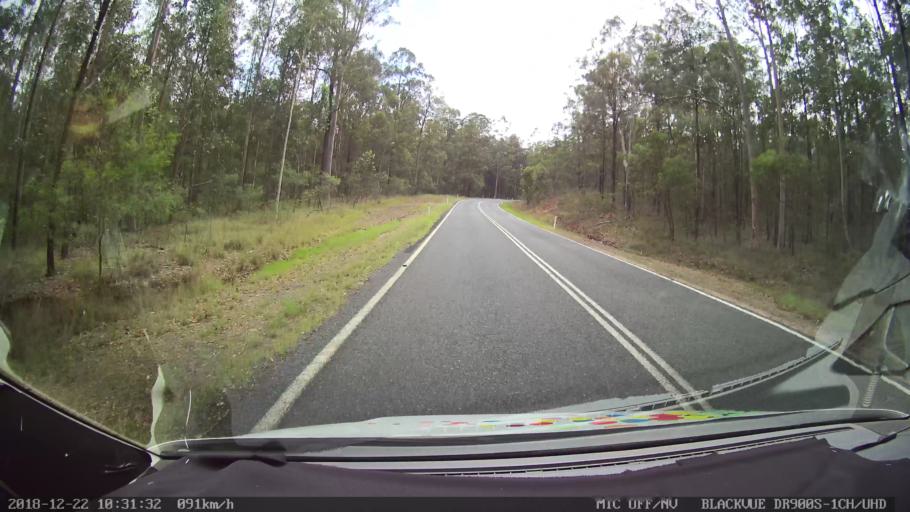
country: AU
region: New South Wales
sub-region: Clarence Valley
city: South Grafton
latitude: -29.6229
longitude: 152.6281
